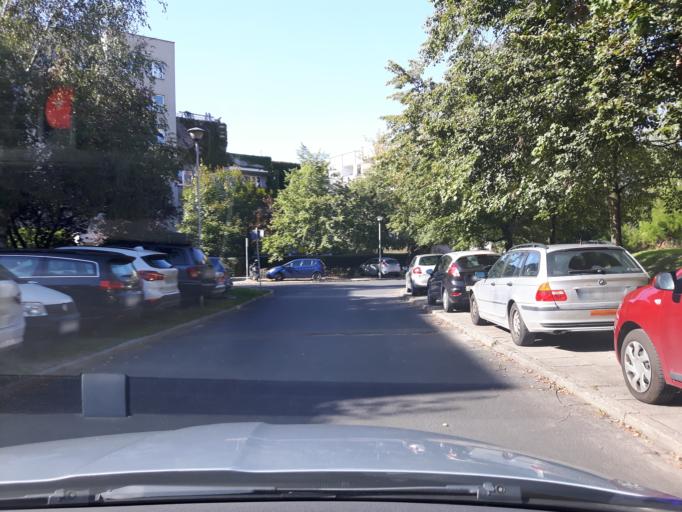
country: PL
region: Masovian Voivodeship
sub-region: Warszawa
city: Praga Poludnie
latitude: 52.2287
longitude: 21.1014
